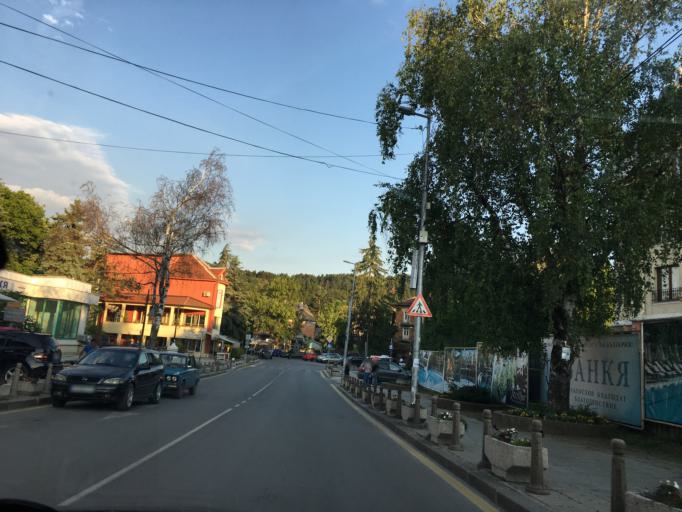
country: BG
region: Sofiya
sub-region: Obshtina Bozhurishte
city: Bozhurishte
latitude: 42.7067
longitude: 23.1475
